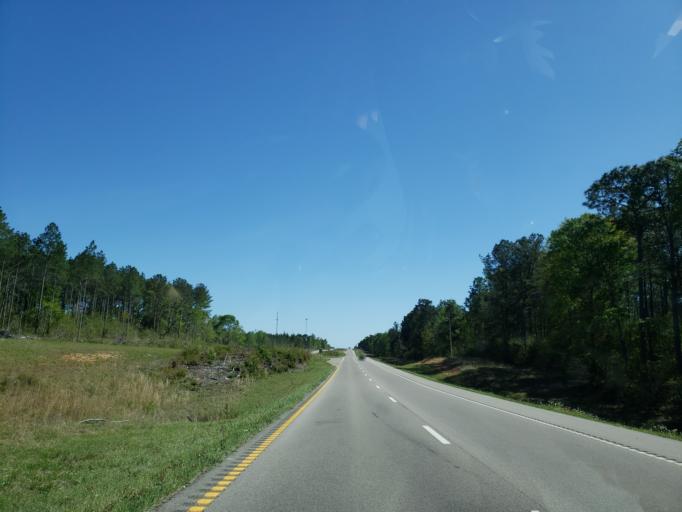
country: US
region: Mississippi
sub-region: Stone County
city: Wiggins
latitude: 30.9662
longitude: -89.1945
